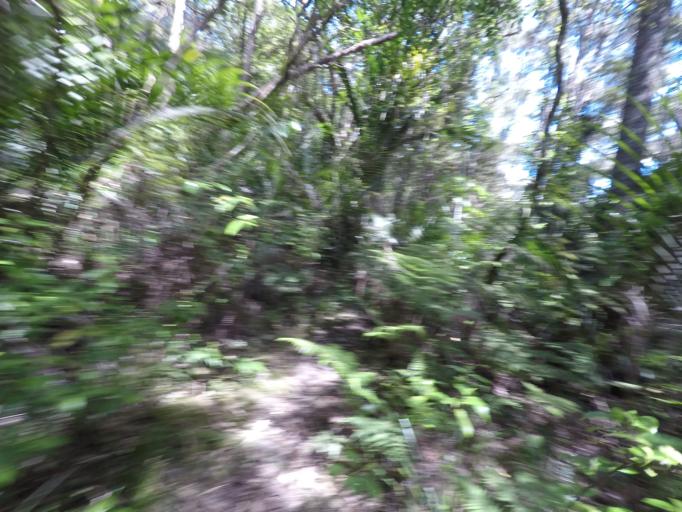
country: NZ
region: Auckland
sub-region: Auckland
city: Titirangi
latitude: -36.9730
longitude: 174.6312
